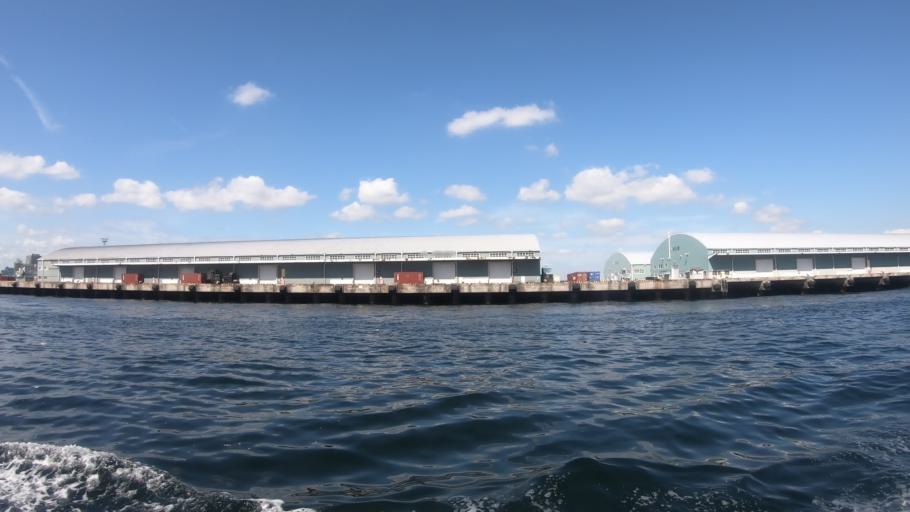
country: JP
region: Kanagawa
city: Yokohama
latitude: 35.4475
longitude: 139.6653
